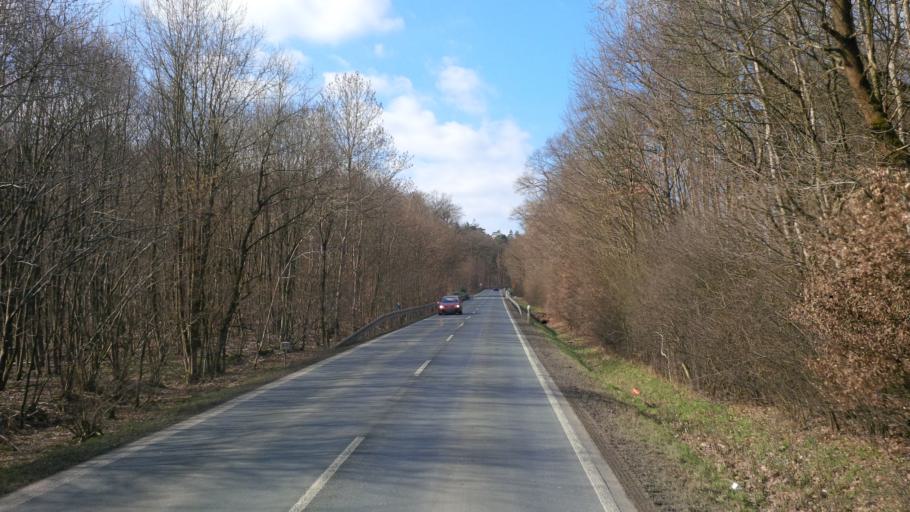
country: DE
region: Hesse
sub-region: Regierungsbezirk Darmstadt
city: Neu-Anspach
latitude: 50.3338
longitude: 8.5080
